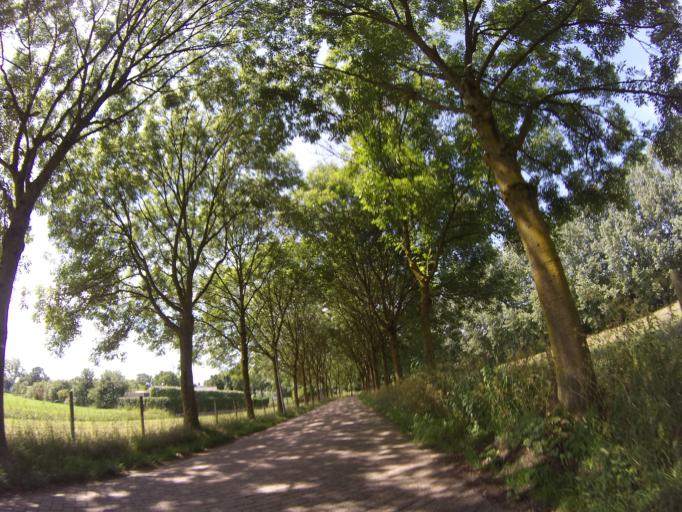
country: NL
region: Utrecht
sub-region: Gemeente Utrecht
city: Lunetten
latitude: 52.0806
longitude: 5.1628
